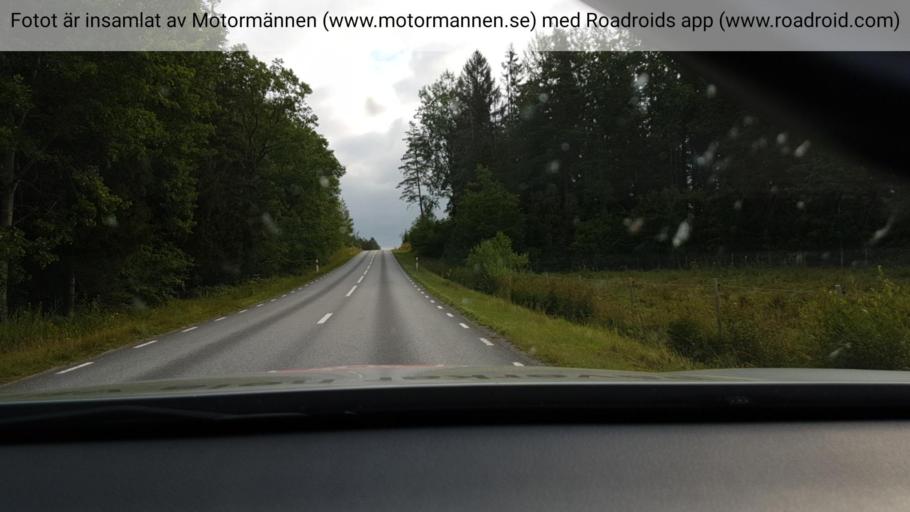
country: SE
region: Stockholm
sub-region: Norrtalje Kommun
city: Rimbo
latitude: 59.7662
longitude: 18.4166
